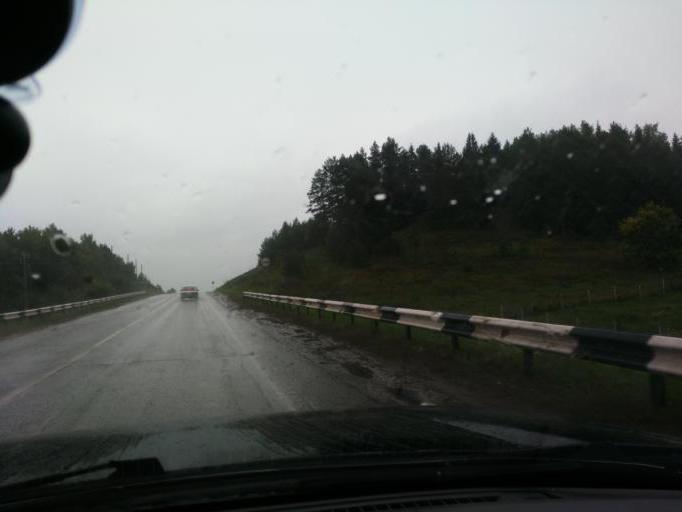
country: RU
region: Perm
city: Osa
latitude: 57.1907
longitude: 55.5912
